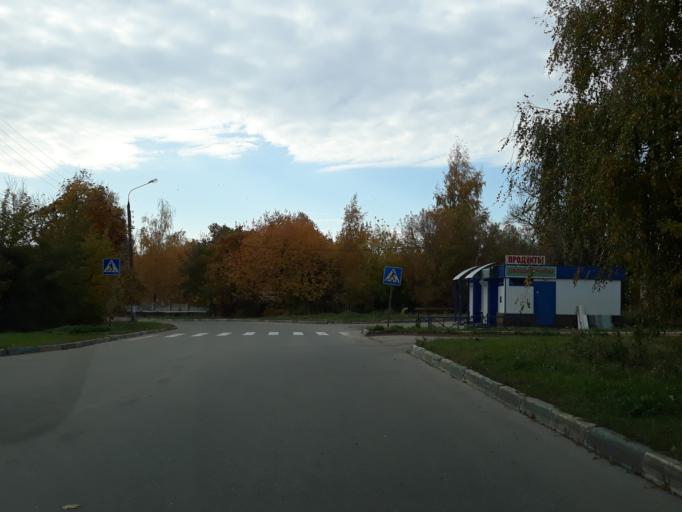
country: RU
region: Nizjnij Novgorod
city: Nizhniy Novgorod
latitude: 56.2379
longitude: 43.9773
